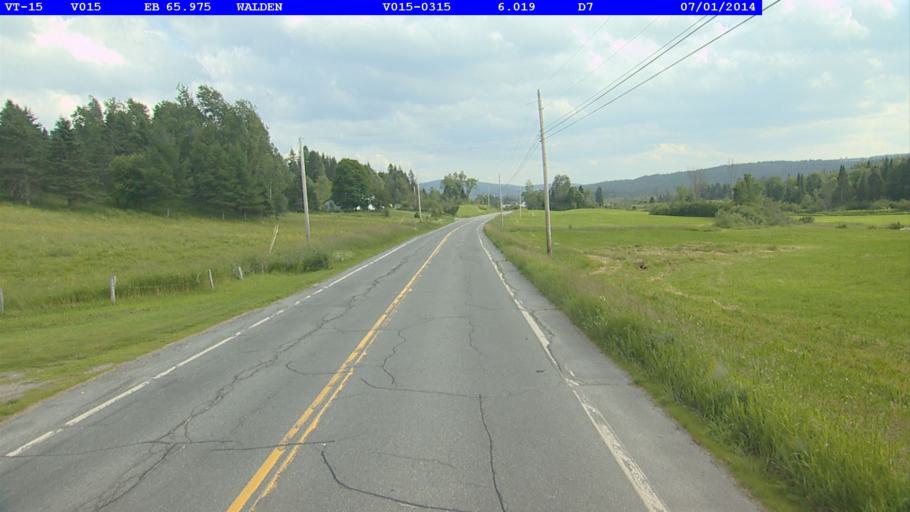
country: US
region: Vermont
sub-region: Caledonia County
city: Hardwick
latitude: 44.4388
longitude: -72.2220
